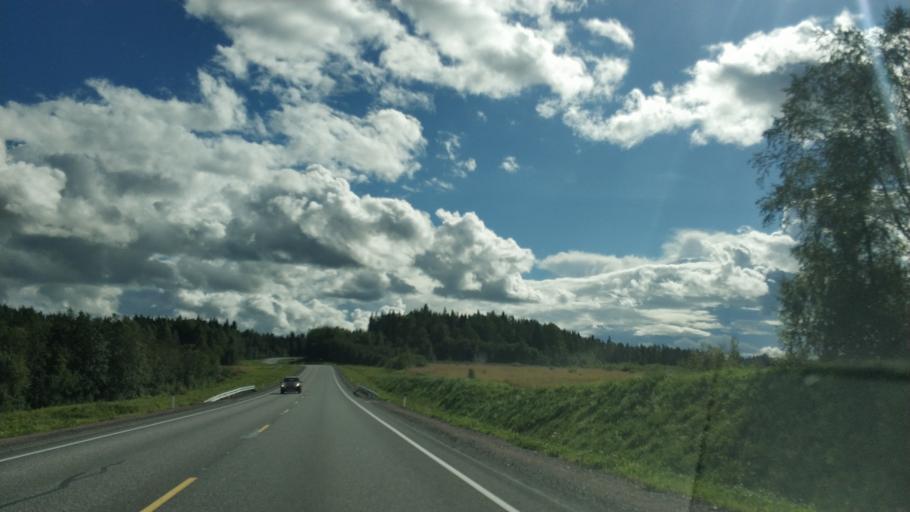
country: RU
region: Republic of Karelia
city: Ruskeala
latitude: 61.8736
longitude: 30.6487
